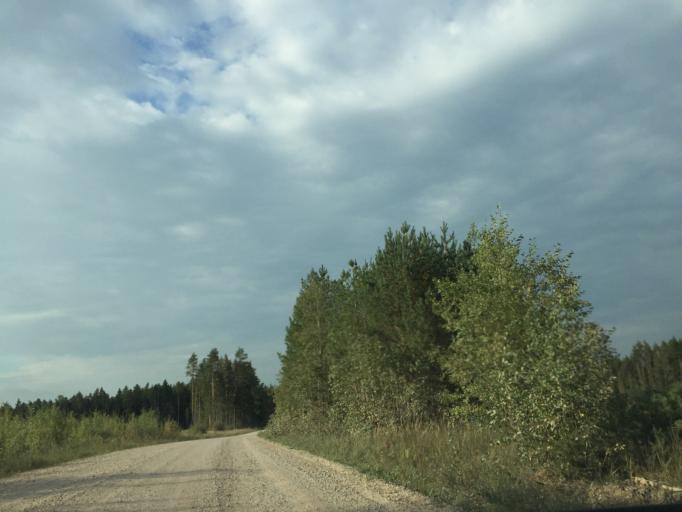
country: LV
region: Baldone
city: Baldone
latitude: 56.7893
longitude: 24.4423
